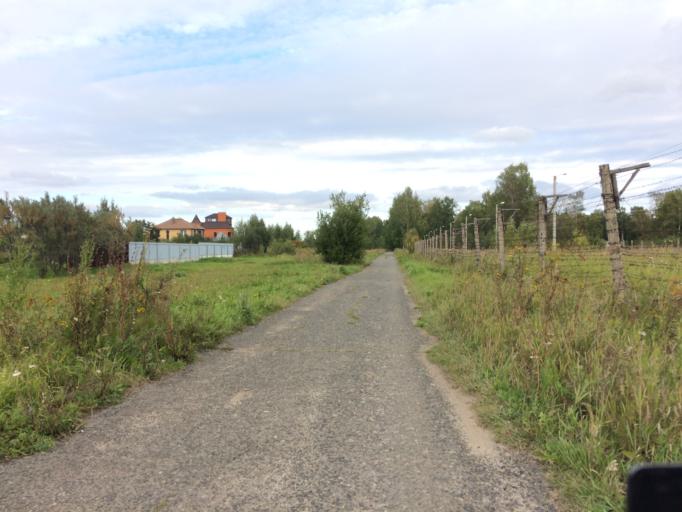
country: RU
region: Mariy-El
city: Yoshkar-Ola
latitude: 56.6590
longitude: 47.9889
